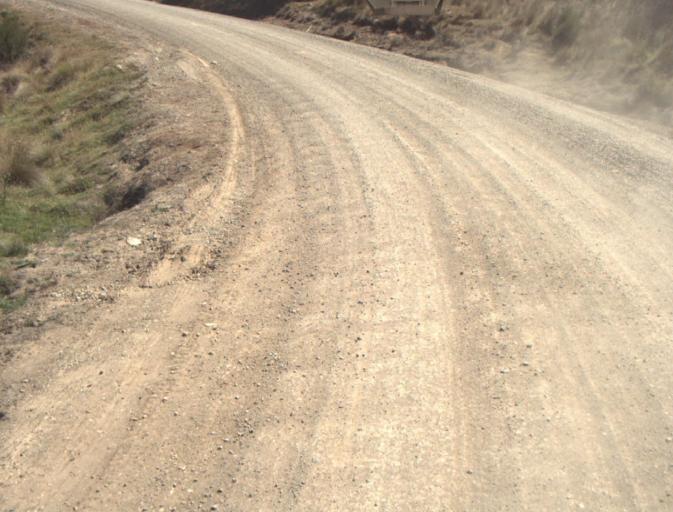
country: AU
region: Tasmania
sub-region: Dorset
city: Scottsdale
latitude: -41.3208
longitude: 147.4622
